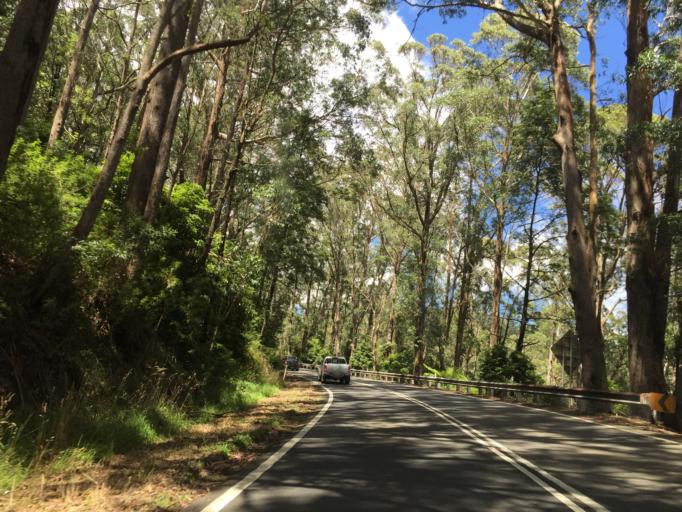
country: AU
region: New South Wales
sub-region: Blue Mountains Municipality
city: Blackheath
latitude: -33.5384
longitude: 150.4192
